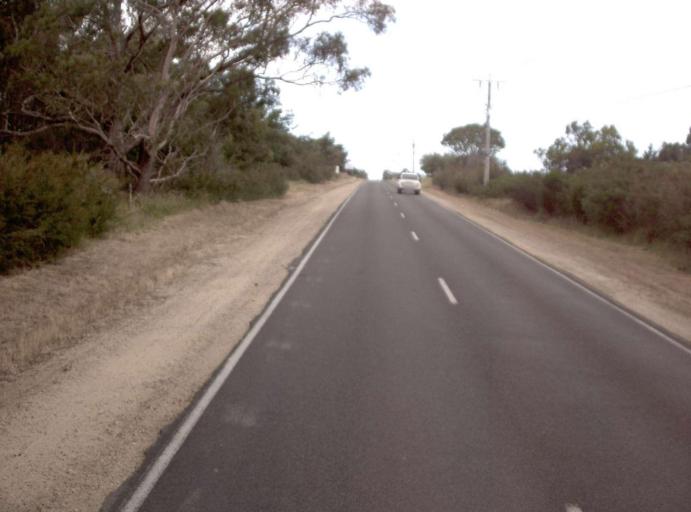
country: AU
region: Victoria
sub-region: Wellington
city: Sale
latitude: -38.1773
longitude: 147.0891
